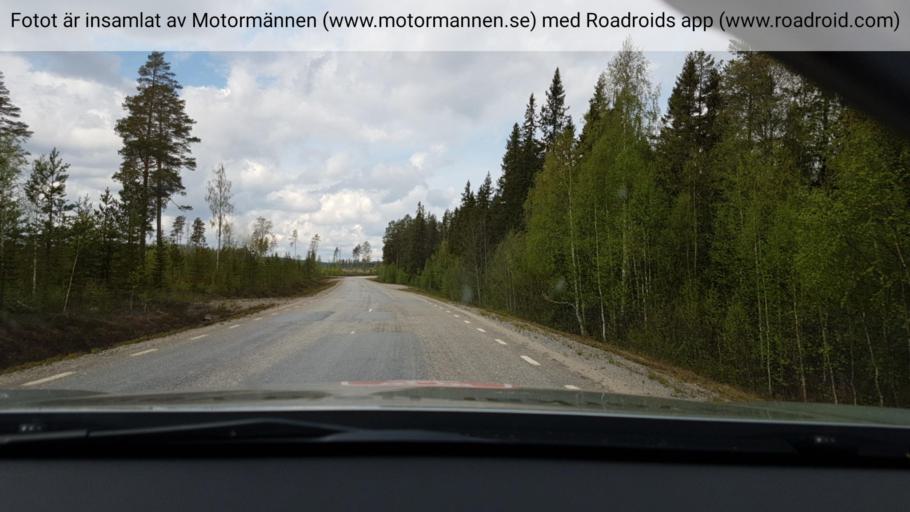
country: SE
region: Vaesternorrland
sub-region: OErnskoeldsviks Kommun
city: Bredbyn
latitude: 63.8911
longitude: 18.5137
